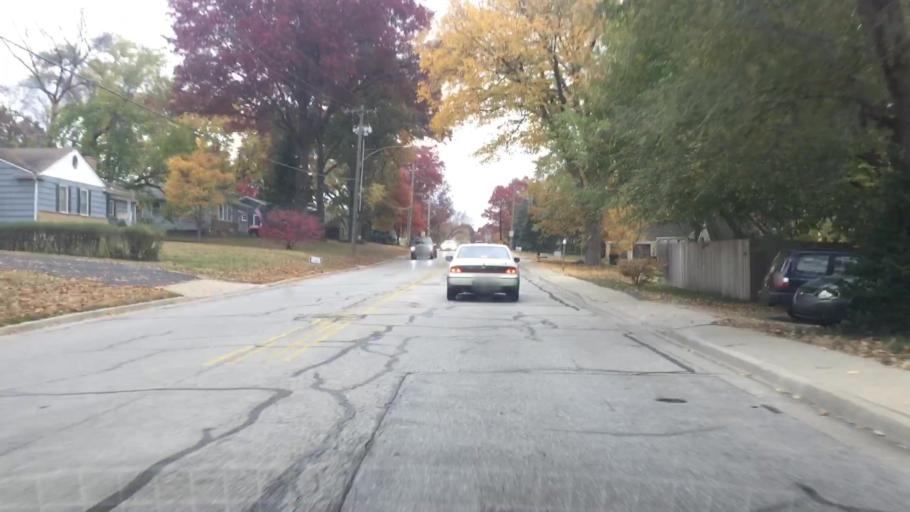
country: US
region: Kansas
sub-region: Johnson County
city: Mission
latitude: 39.0171
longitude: -94.6583
